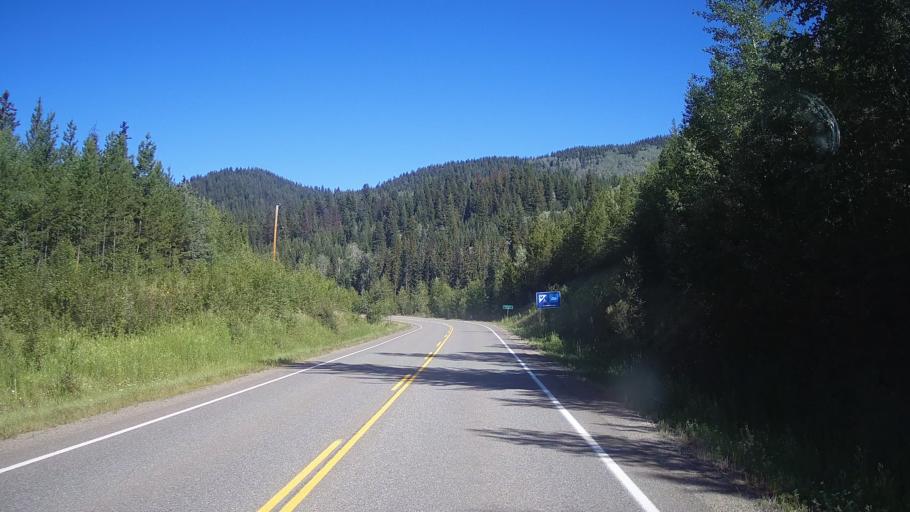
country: CA
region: British Columbia
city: Kamloops
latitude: 51.4678
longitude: -120.5325
